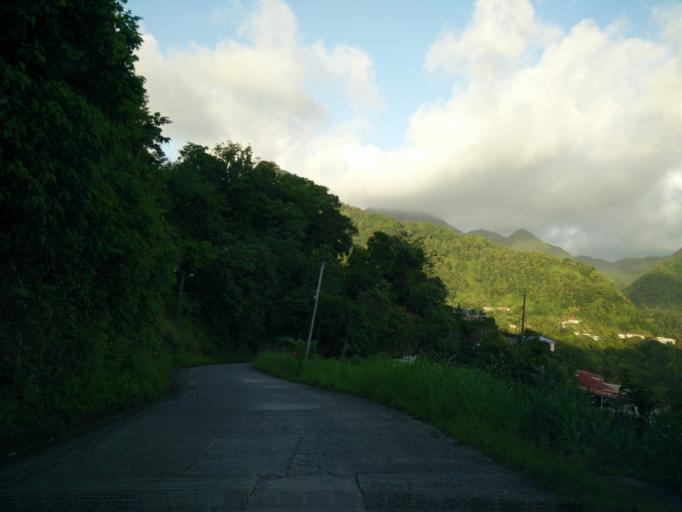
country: MQ
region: Martinique
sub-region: Martinique
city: Le Morne-Rouge
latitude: 14.7373
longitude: -61.1405
